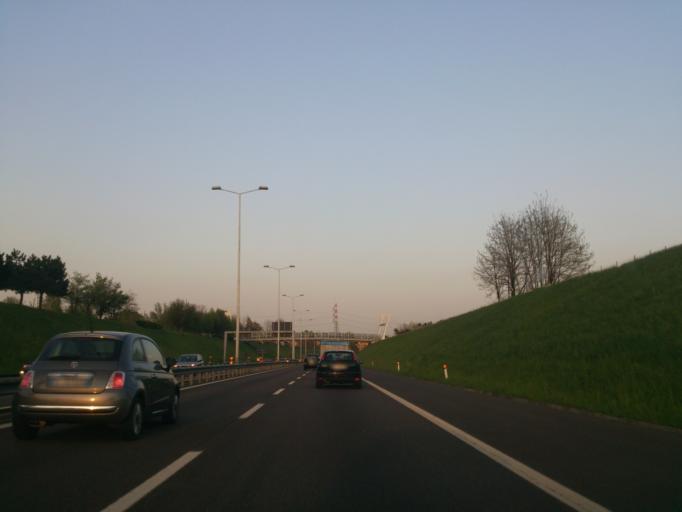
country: IT
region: Lombardy
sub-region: Provincia di Monza e Brianza
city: Nova Milanese
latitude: 45.5766
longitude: 9.2124
